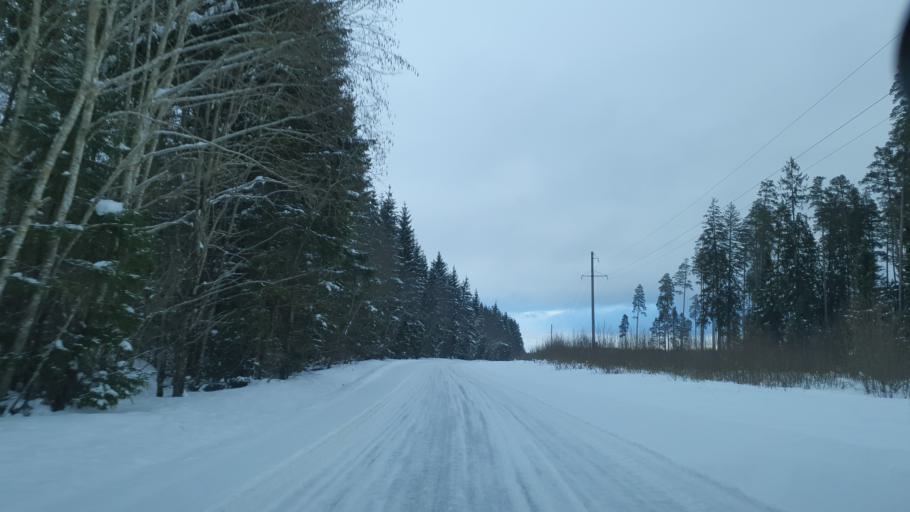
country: EE
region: Polvamaa
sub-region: Polva linn
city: Polva
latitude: 58.1433
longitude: 27.0994
